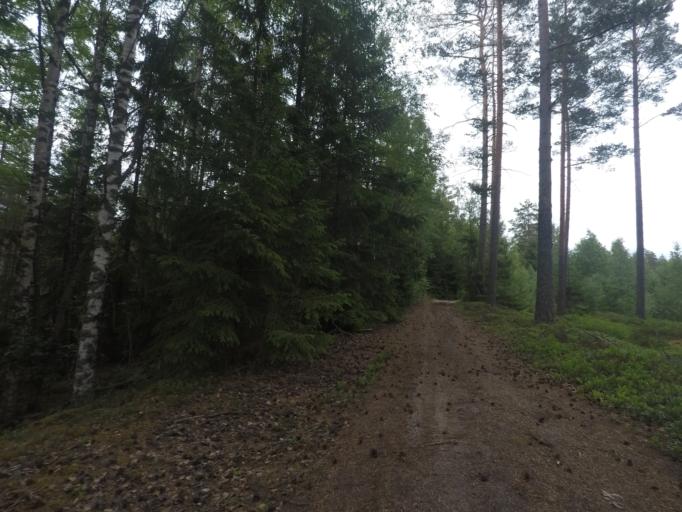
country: SE
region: Vaestmanland
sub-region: Kungsors Kommun
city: Kungsoer
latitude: 59.3717
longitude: 16.1036
